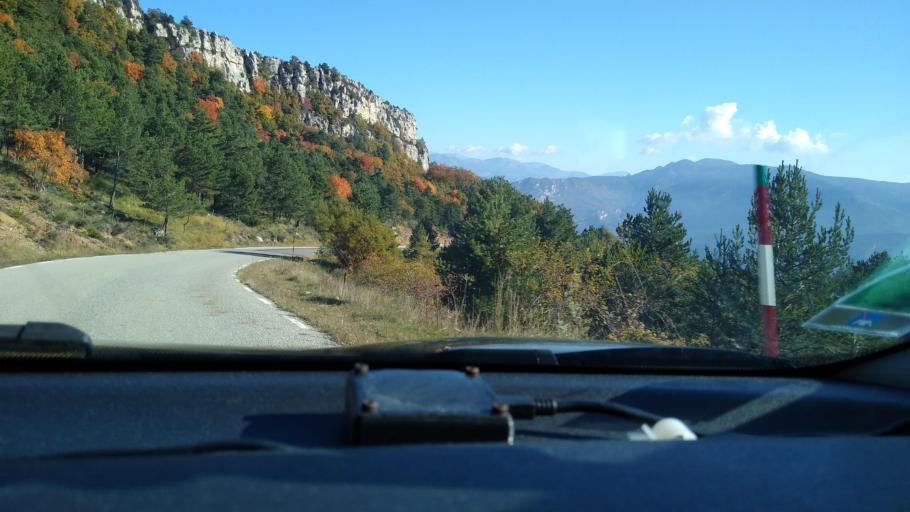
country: ES
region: Catalonia
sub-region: Provincia de Barcelona
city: Vallcebre
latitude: 42.1800
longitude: 1.8168
